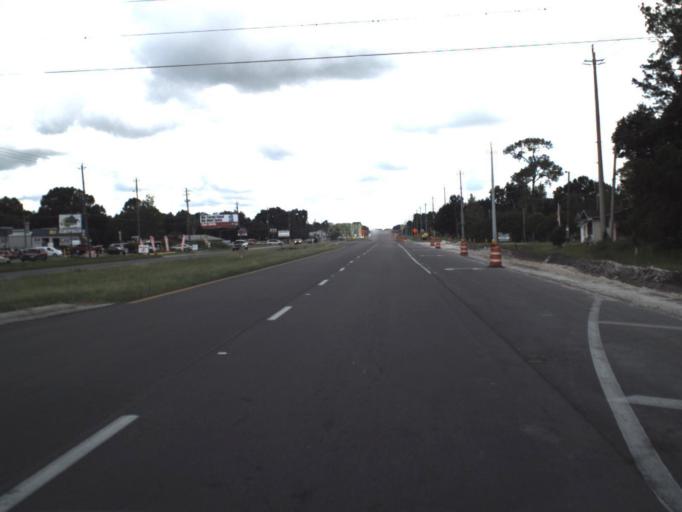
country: US
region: Florida
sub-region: Polk County
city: Gibsonia
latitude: 28.1402
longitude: -81.9735
